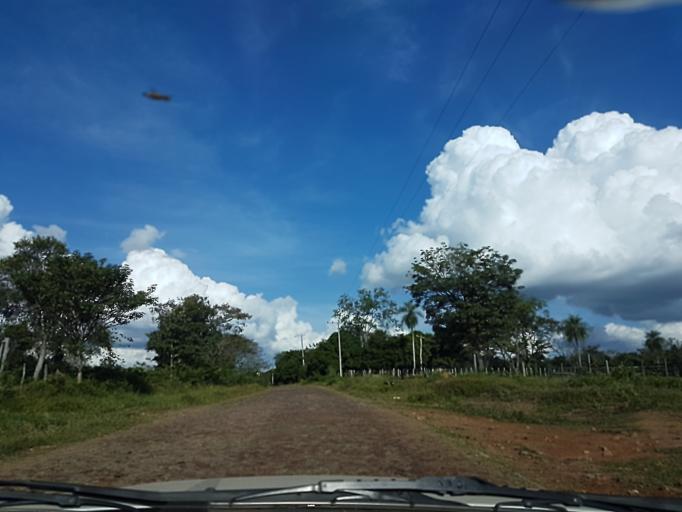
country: PY
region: Cordillera
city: Arroyos y Esteros
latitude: -24.9949
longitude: -57.1877
